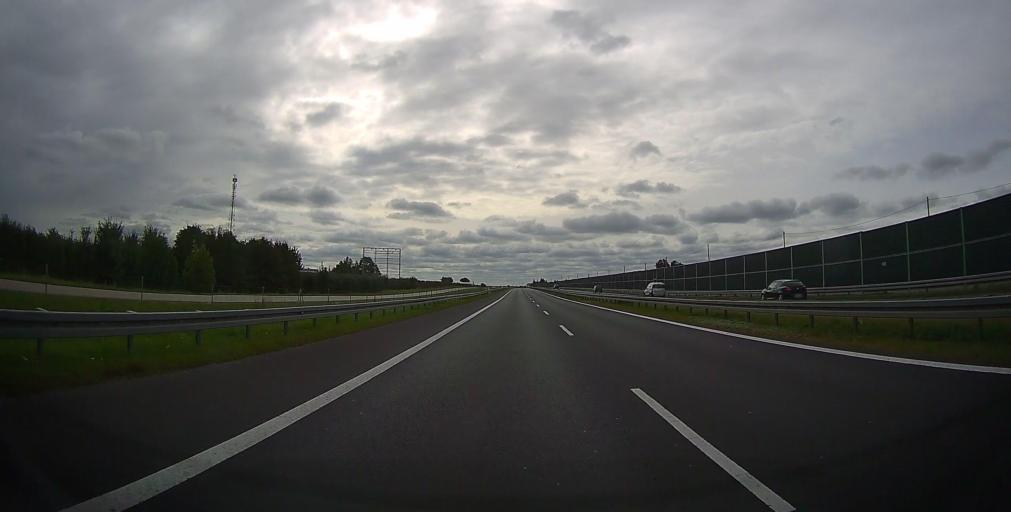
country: PL
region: Masovian Voivodeship
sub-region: Powiat grojecki
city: Jasieniec
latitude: 51.7788
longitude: 20.8967
